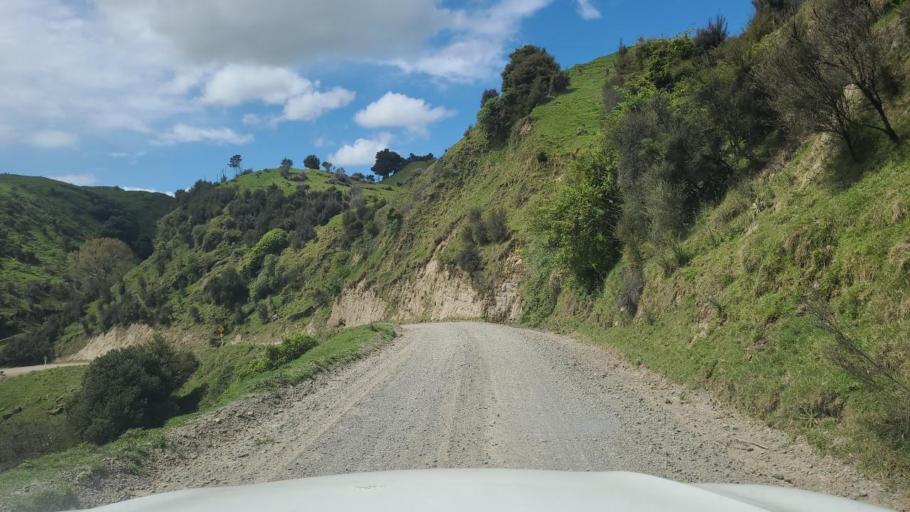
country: NZ
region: Hawke's Bay
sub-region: Napier City
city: Taradale
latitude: -39.2684
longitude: 176.6629
